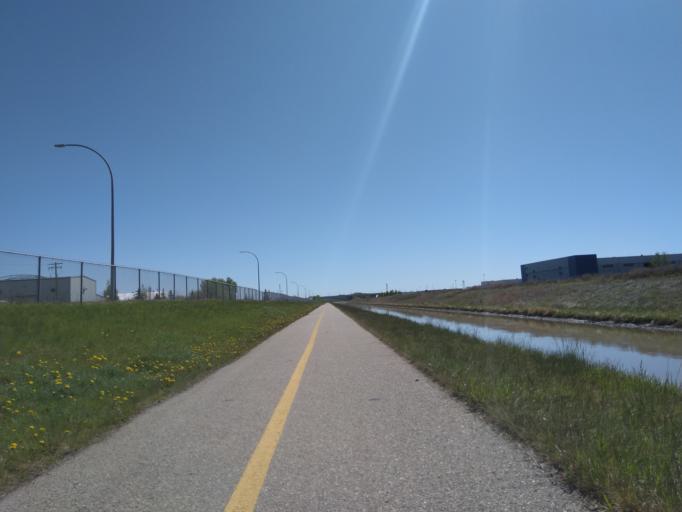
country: CA
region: Alberta
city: Calgary
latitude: 50.9653
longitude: -113.9752
